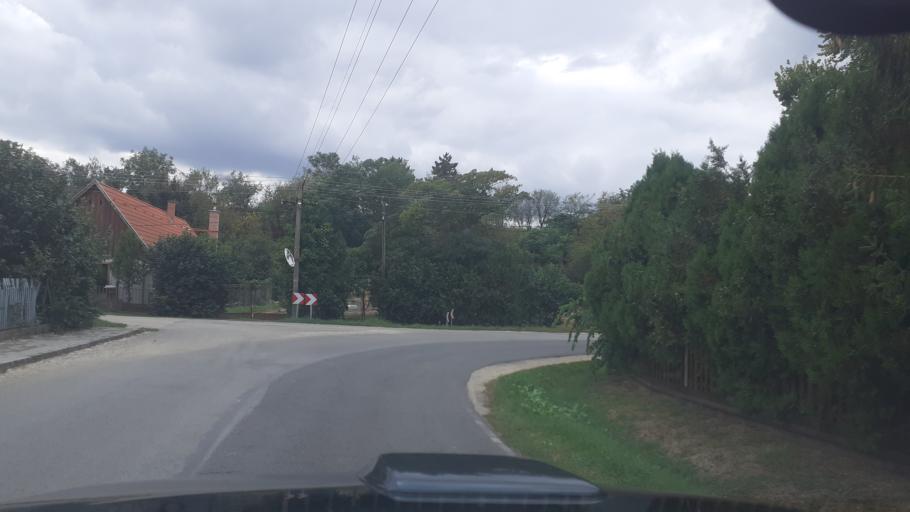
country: HU
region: Fejer
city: Racalmas
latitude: 47.0527
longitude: 18.9183
